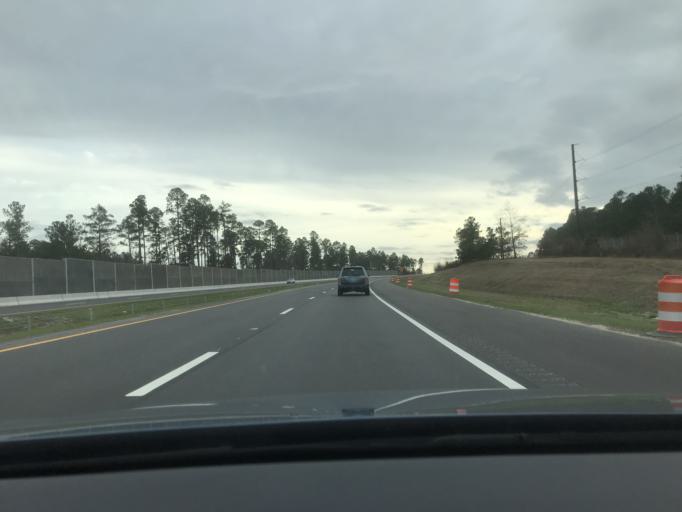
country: US
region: North Carolina
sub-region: Cumberland County
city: Fort Bragg
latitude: 35.0763
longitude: -79.0207
